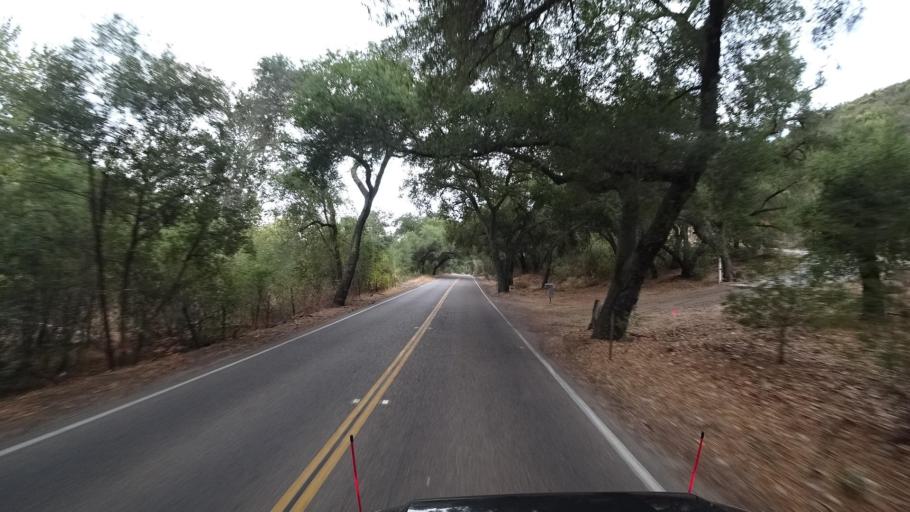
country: US
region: California
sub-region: San Diego County
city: Ramona
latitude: 32.9889
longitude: -116.9267
